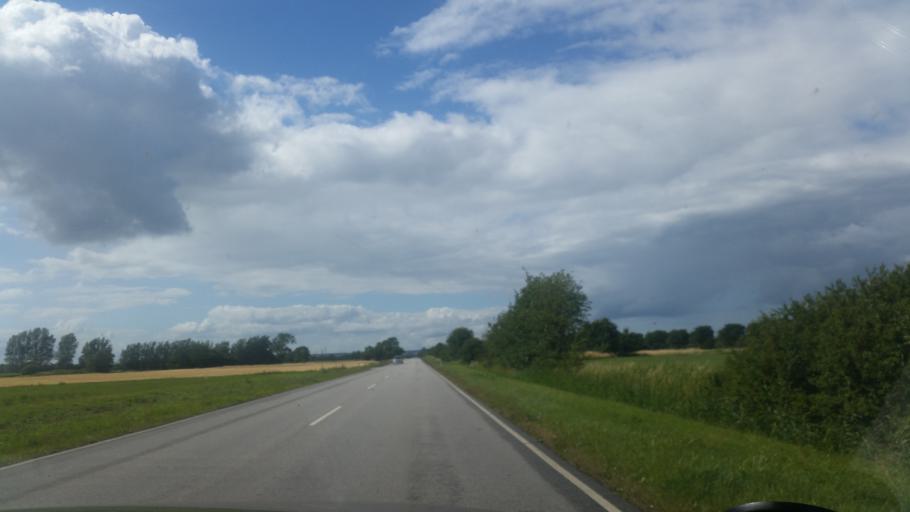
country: DK
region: Zealand
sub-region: Holbaek Kommune
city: Svinninge
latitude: 55.7487
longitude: 11.5269
